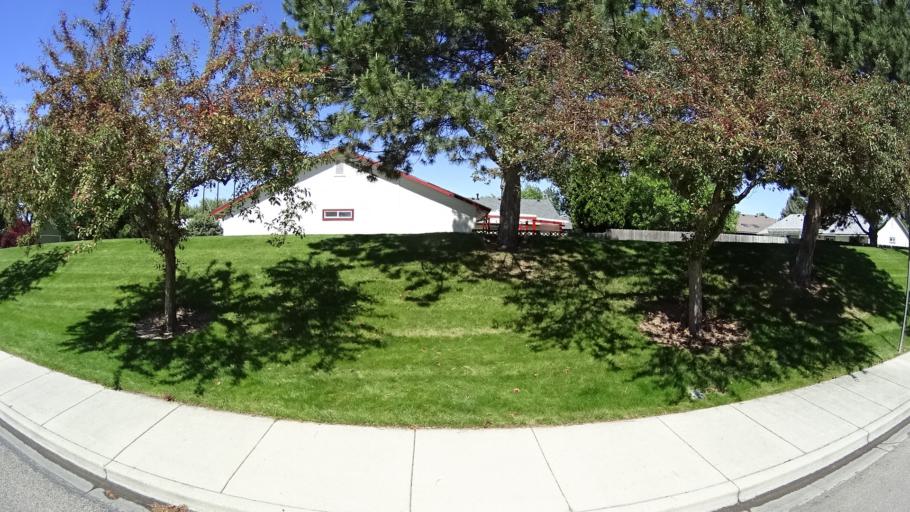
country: US
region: Idaho
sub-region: Ada County
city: Boise
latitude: 43.5505
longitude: -116.1383
